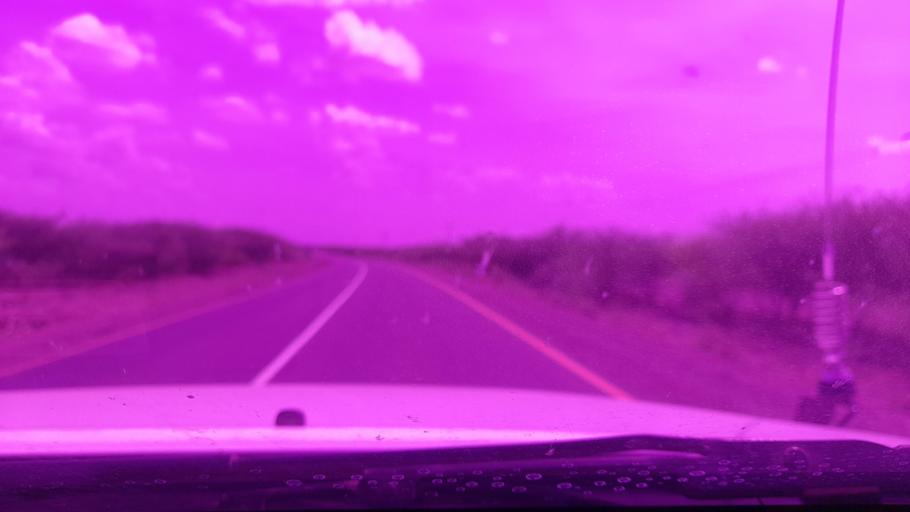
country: ET
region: Afar
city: Awash
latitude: 9.3570
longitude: 40.3046
